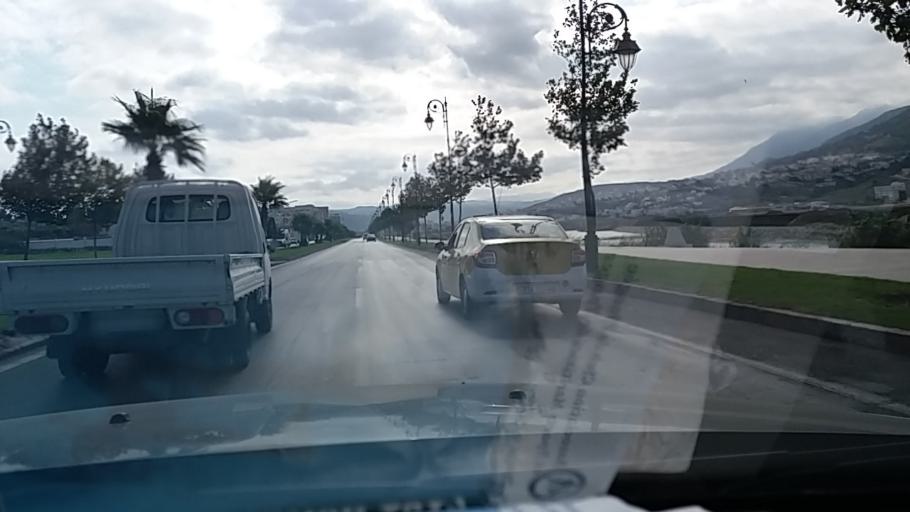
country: MA
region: Tanger-Tetouan
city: Tetouan
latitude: 35.5650
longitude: -5.3813
